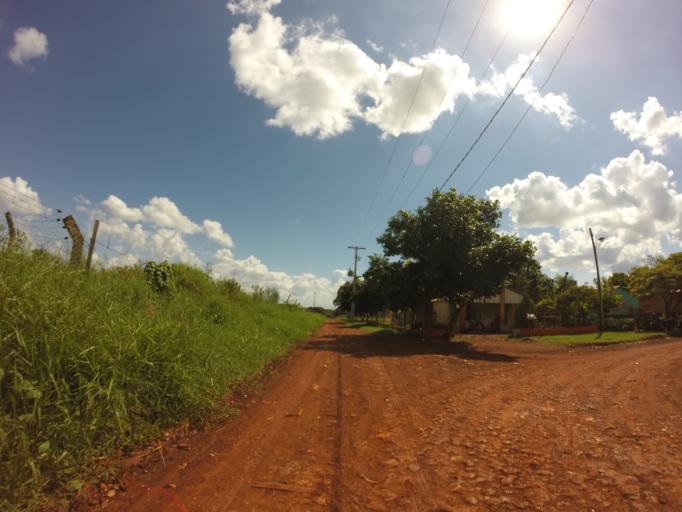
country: PY
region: Alto Parana
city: Ciudad del Este
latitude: -25.3768
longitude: -54.6569
